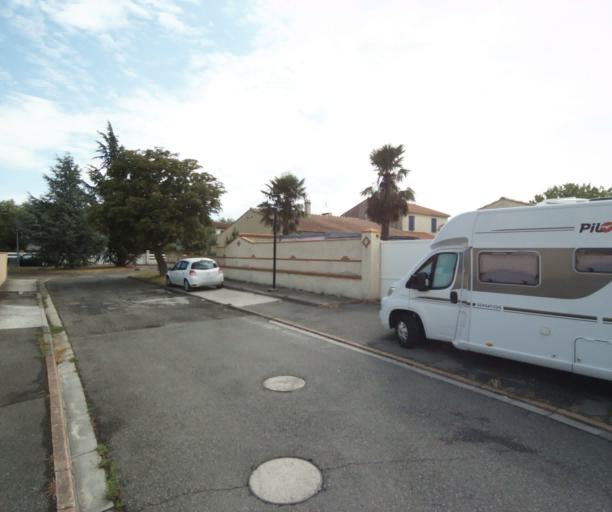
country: FR
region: Midi-Pyrenees
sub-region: Departement de la Haute-Garonne
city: Revel
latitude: 43.4620
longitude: 1.9909
